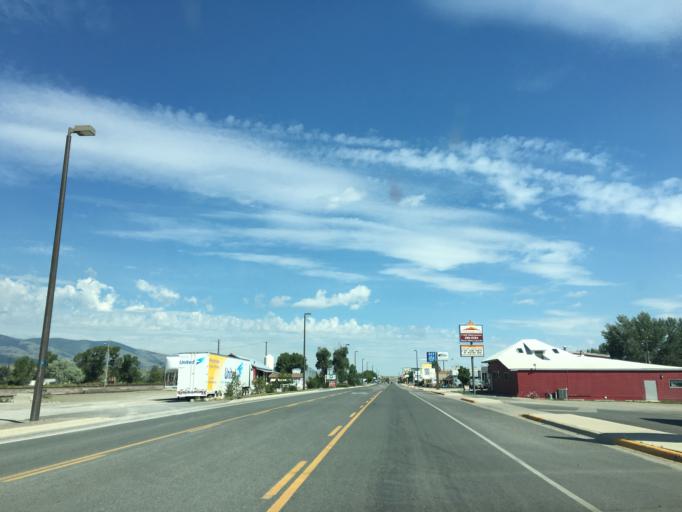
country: US
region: Montana
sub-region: Broadwater County
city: Townsend
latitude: 46.3207
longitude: -111.5224
